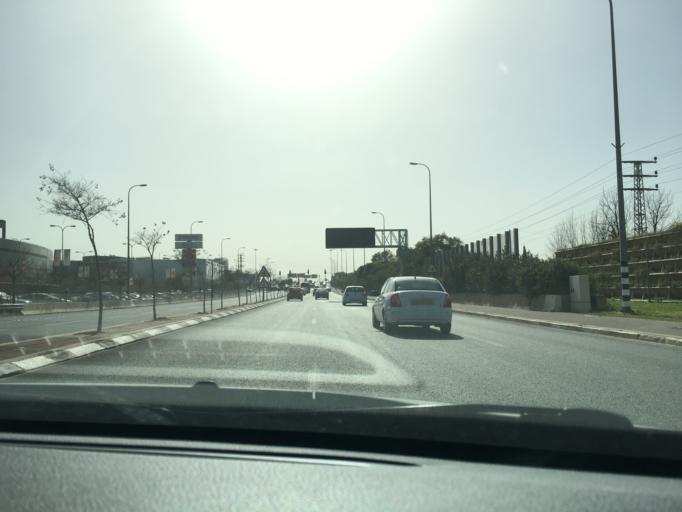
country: IL
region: Central District
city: Kfar Saba
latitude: 32.1688
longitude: 34.9285
